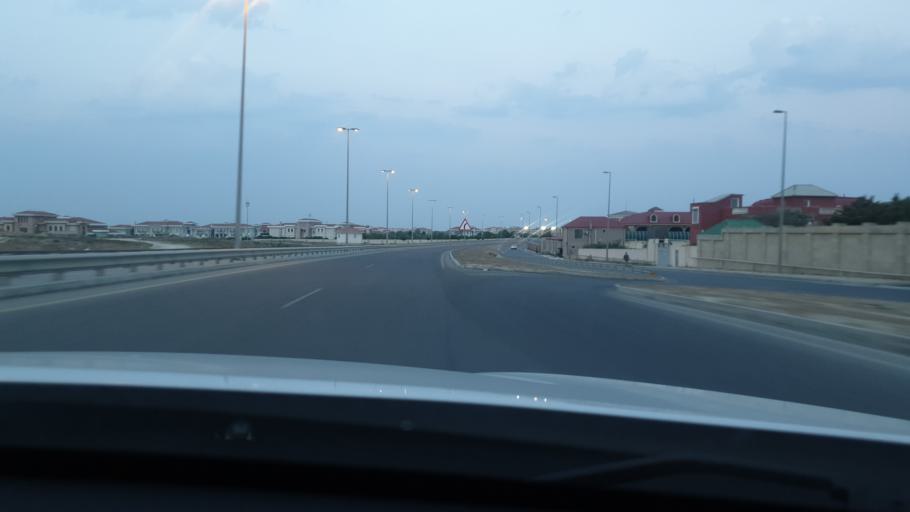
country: AZ
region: Baki
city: Bilajer
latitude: 40.5892
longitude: 50.0529
